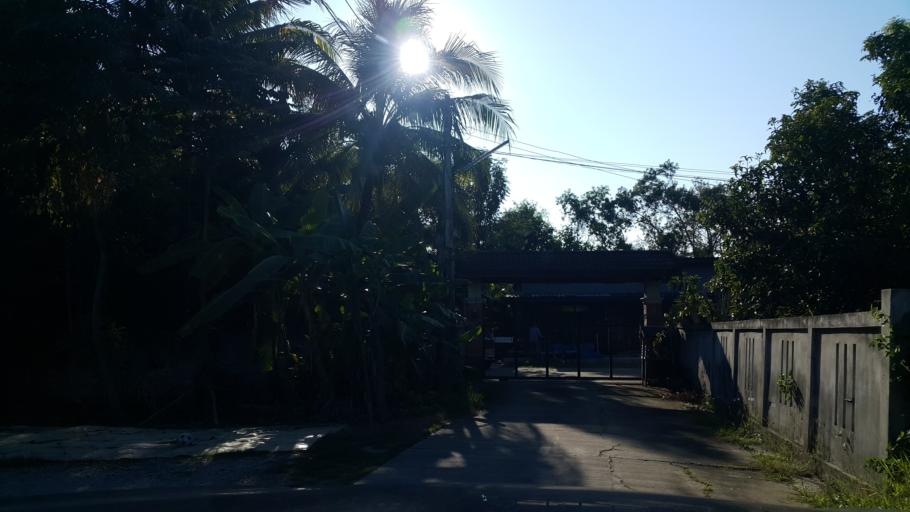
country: TH
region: Chiang Mai
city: Saraphi
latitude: 18.7532
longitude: 99.0514
